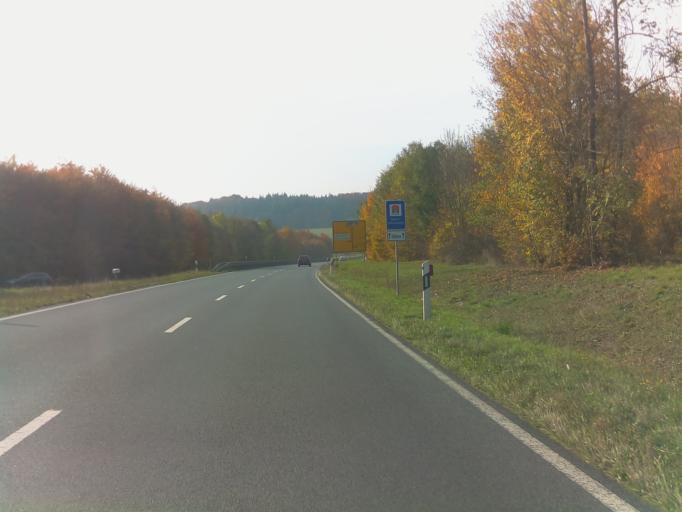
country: DE
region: Baden-Wuerttemberg
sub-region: Regierungsbezirk Stuttgart
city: Assamstadt
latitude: 49.4417
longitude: 9.7261
